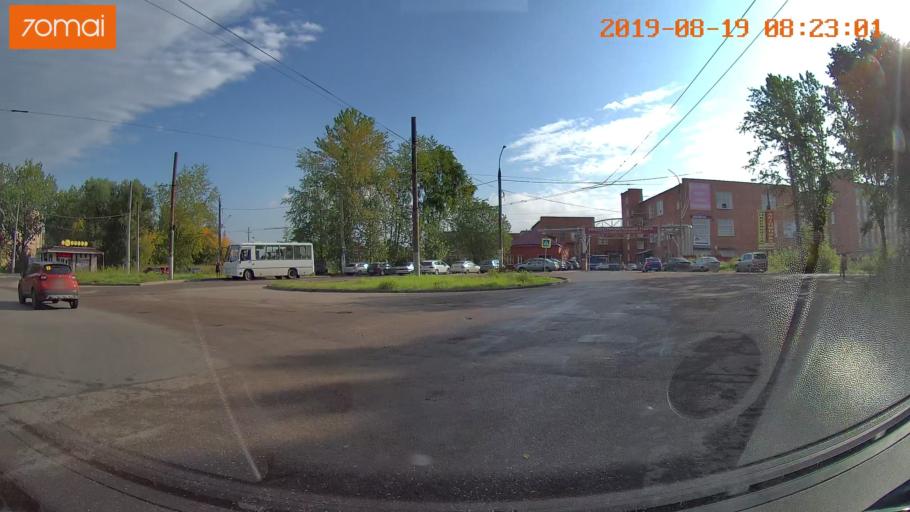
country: RU
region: Ivanovo
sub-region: Gorod Ivanovo
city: Ivanovo
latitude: 56.9844
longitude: 41.0178
